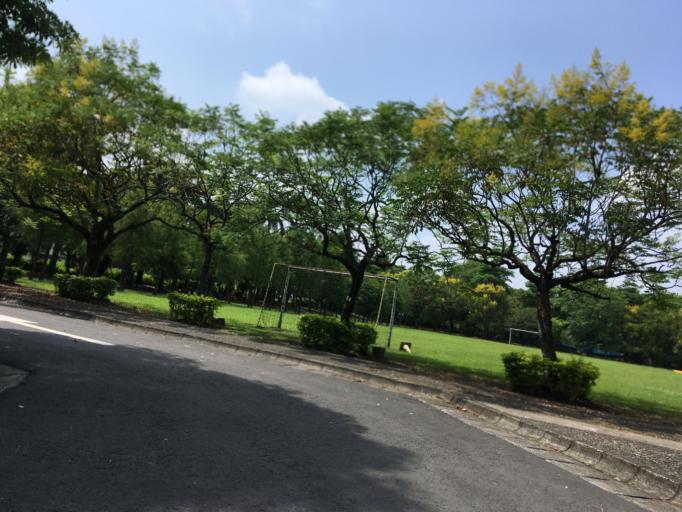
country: TW
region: Taiwan
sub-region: Yilan
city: Yilan
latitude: 24.6795
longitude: 121.6889
